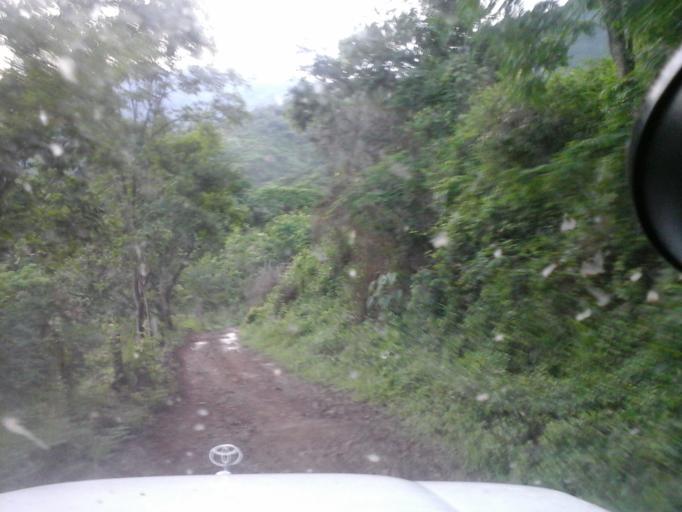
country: CO
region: Cesar
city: Agustin Codazzi
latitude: 10.1737
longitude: -73.1472
